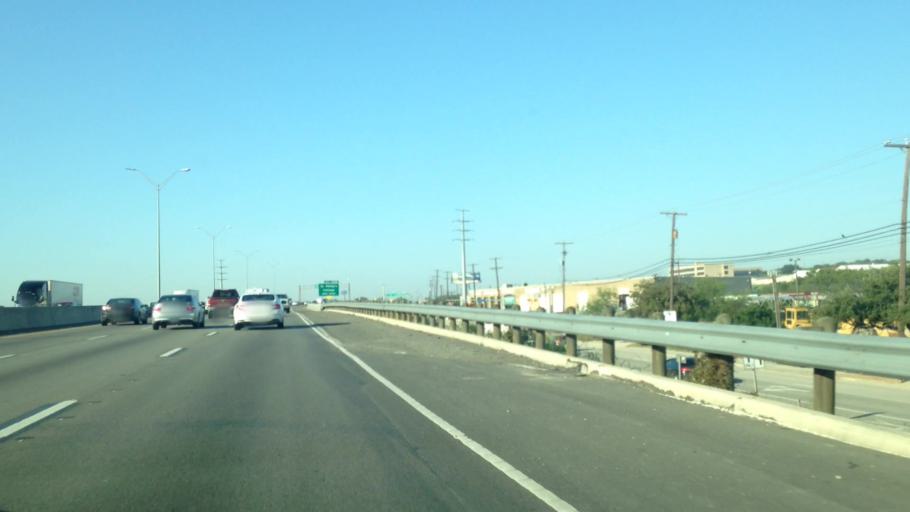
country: US
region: Texas
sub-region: Bexar County
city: Terrell Hills
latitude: 29.4427
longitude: -98.4371
